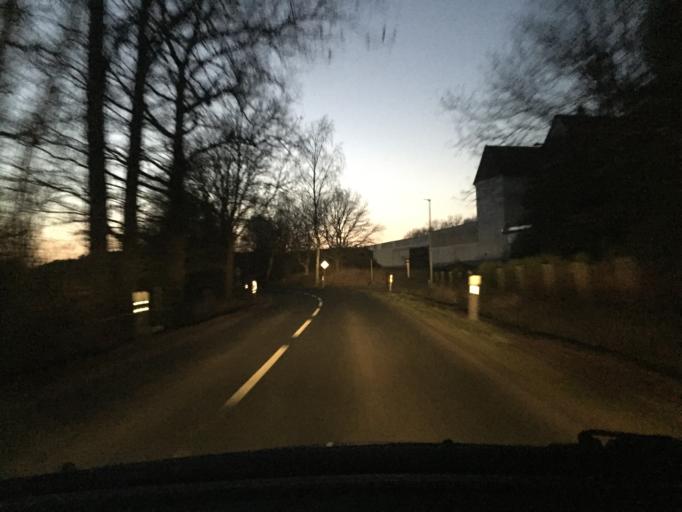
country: DE
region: Lower Saxony
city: Nahrendorf
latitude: 53.1666
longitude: 10.8496
